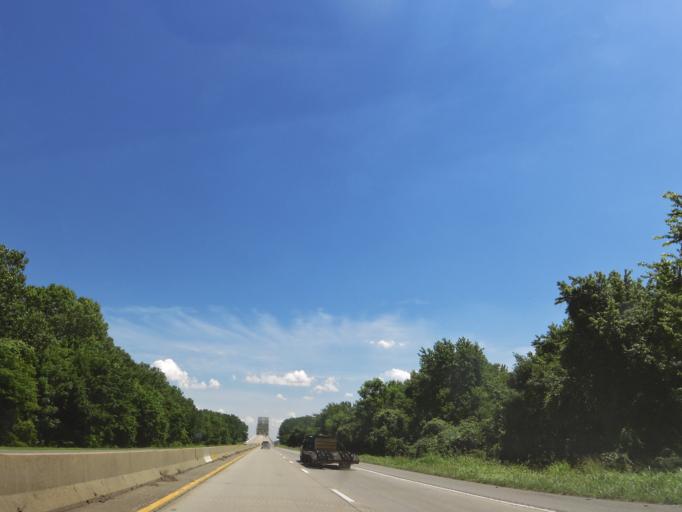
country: US
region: Missouri
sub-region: Pemiscot County
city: Caruthersville
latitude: 36.1244
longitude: -89.6185
